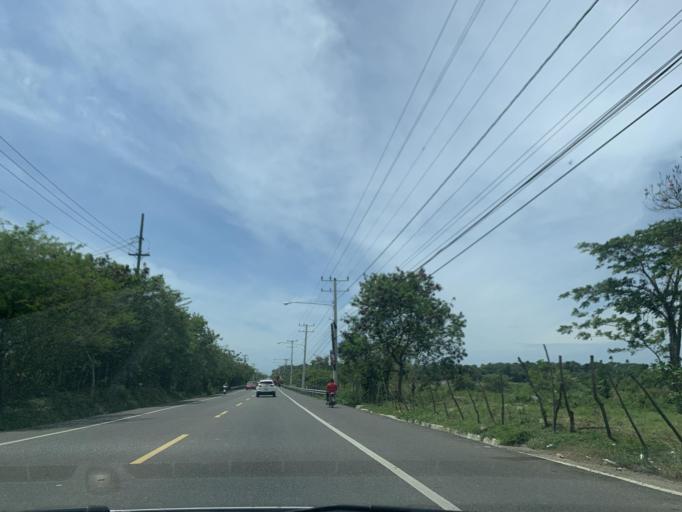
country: DO
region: Puerto Plata
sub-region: Puerto Plata
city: Puerto Plata
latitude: 19.7407
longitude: -70.6332
